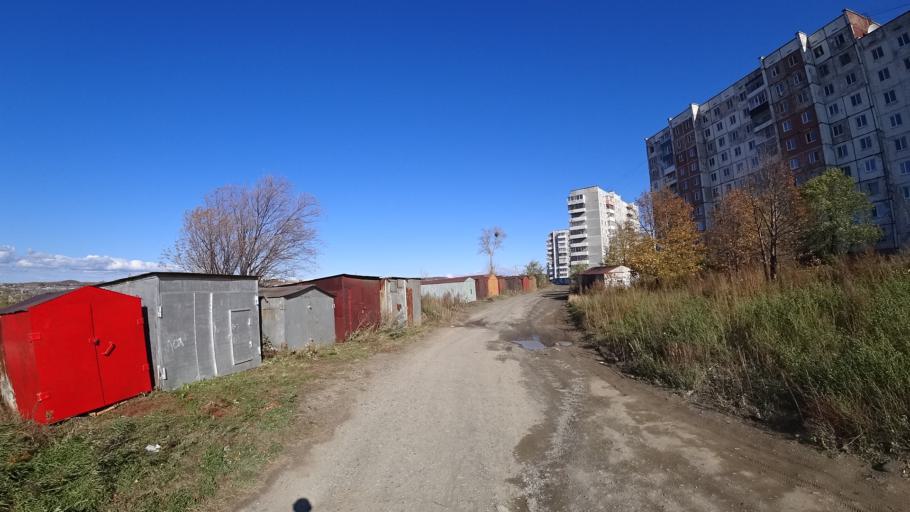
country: RU
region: Khabarovsk Krai
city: Amursk
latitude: 50.2182
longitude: 136.8912
